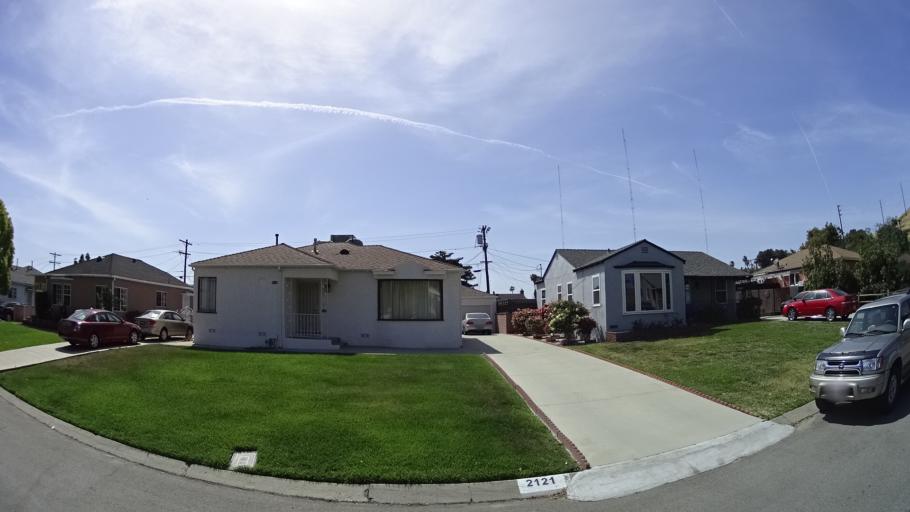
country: US
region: California
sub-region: Los Angeles County
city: Belvedere
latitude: 34.0686
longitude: -118.1909
